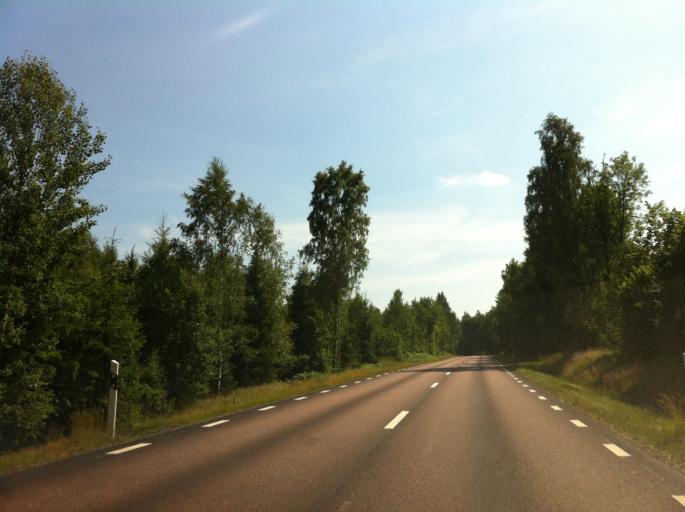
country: SE
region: Kalmar
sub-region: Nybro Kommun
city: Nybro
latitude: 56.8045
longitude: 15.7866
